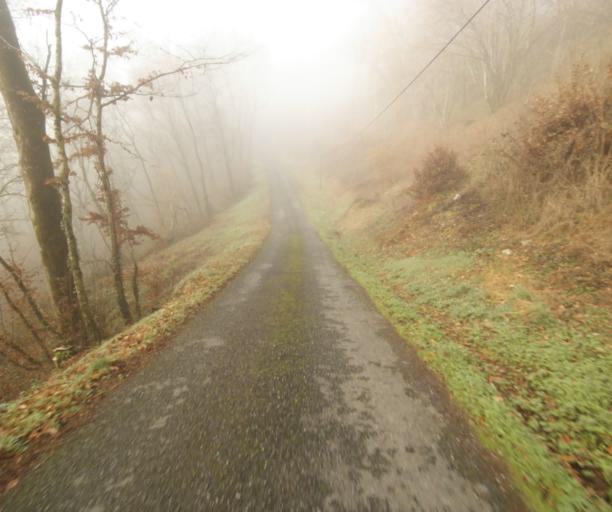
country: FR
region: Limousin
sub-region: Departement de la Correze
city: Tulle
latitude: 45.2620
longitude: 1.7854
